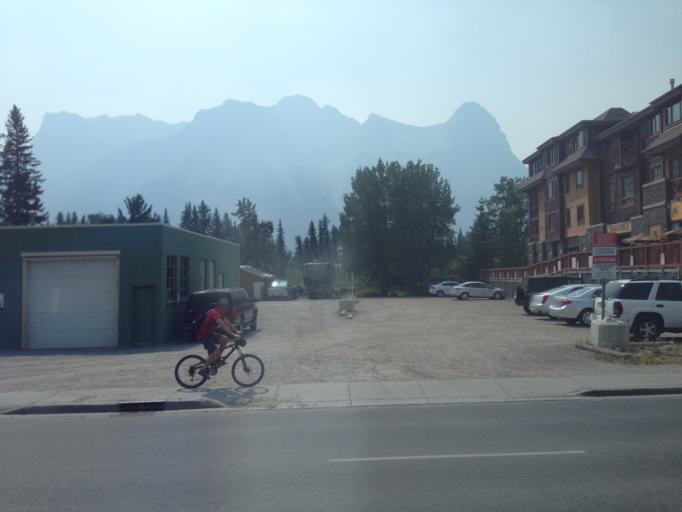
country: CA
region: Alberta
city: Canmore
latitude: 51.0891
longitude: -115.3530
